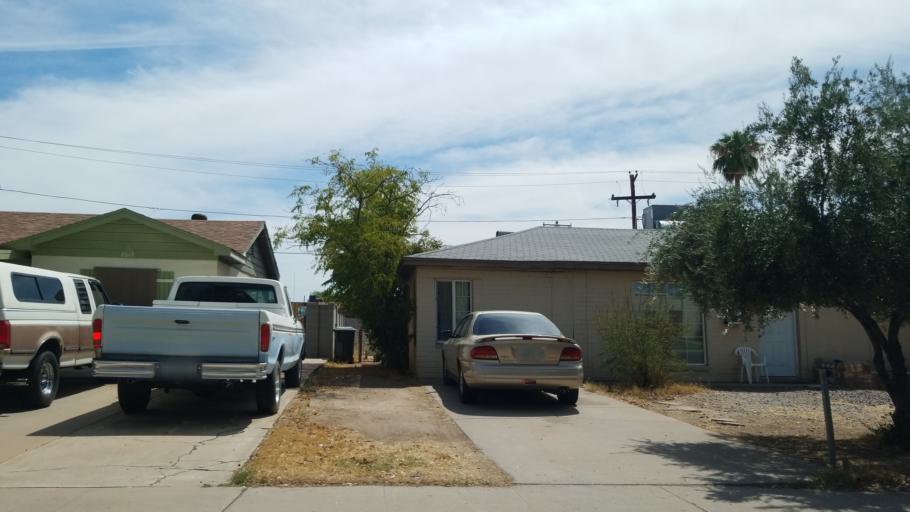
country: US
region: Arizona
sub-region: Maricopa County
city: Glendale
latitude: 33.5539
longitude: -112.1256
